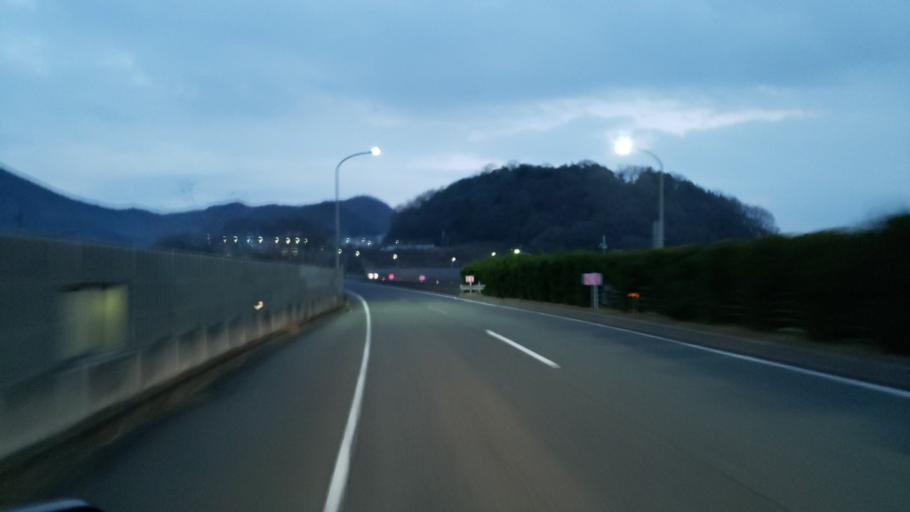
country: JP
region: Hyogo
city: Himeji
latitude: 34.8752
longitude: 134.7387
